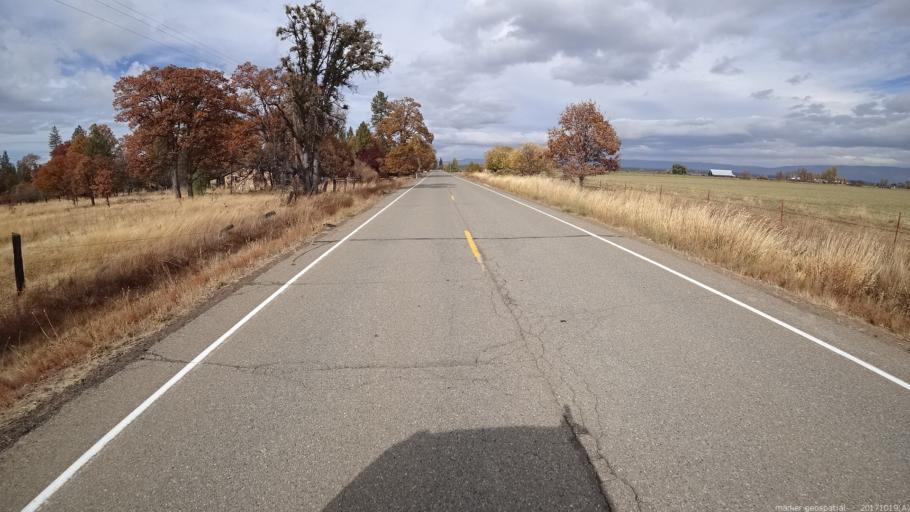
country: US
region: California
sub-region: Shasta County
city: Burney
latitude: 41.0857
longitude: -121.5144
